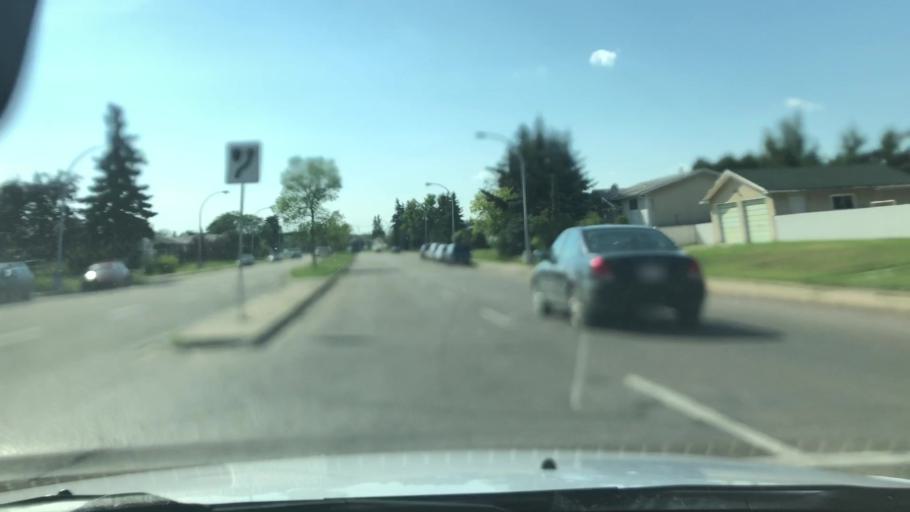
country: CA
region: Alberta
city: Edmonton
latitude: 53.6064
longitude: -113.4852
